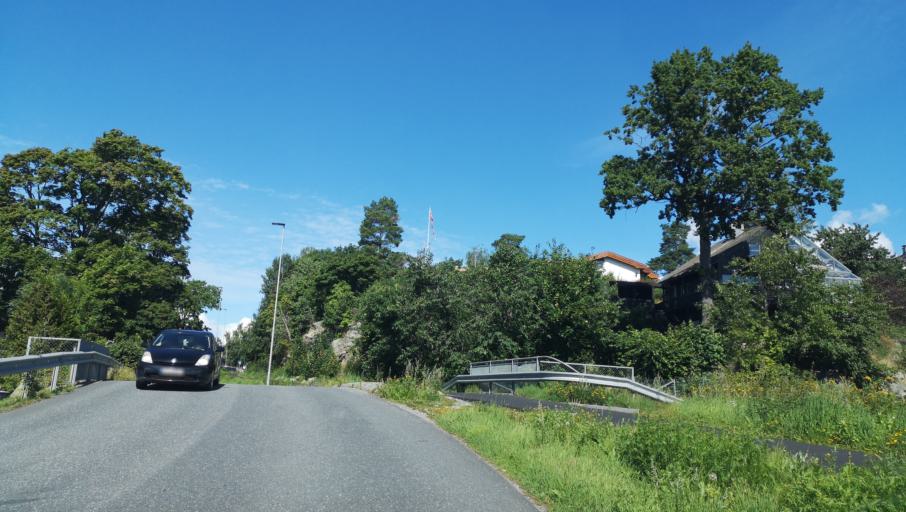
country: NO
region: Akershus
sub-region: Frogn
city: Drobak
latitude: 59.6573
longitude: 10.6417
